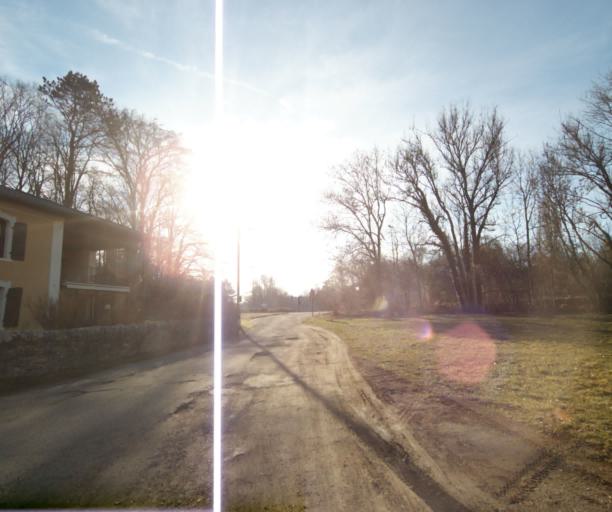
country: FR
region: Lorraine
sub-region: Departement de Meurthe-et-Moselle
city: Chavigny
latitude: 48.6593
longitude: 6.1171
